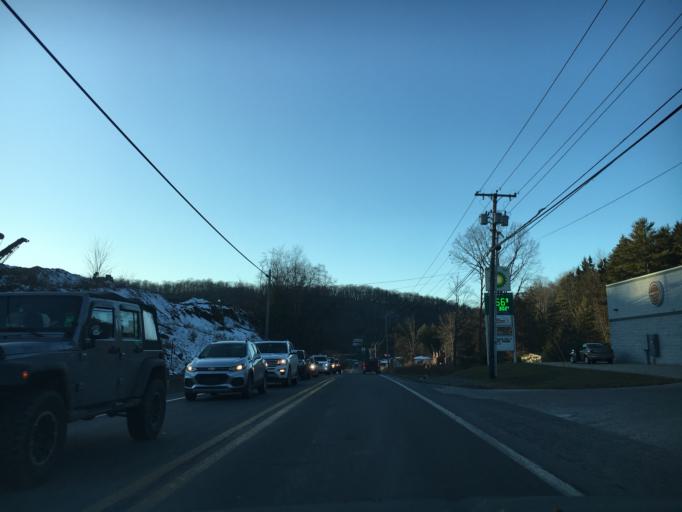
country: US
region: West Virginia
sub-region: Raleigh County
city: Daniels
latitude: 37.7284
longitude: -81.1061
